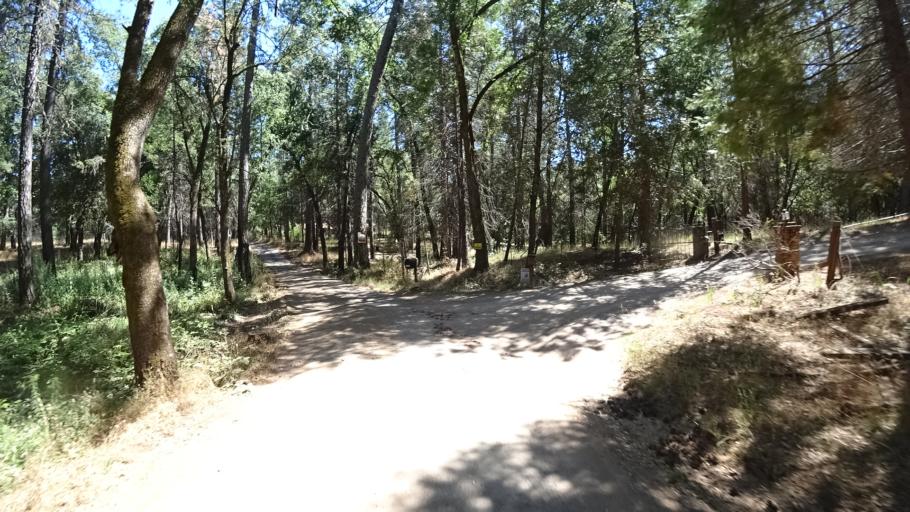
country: US
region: California
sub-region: Calaveras County
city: Mountain Ranch
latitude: 38.2815
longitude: -120.5823
